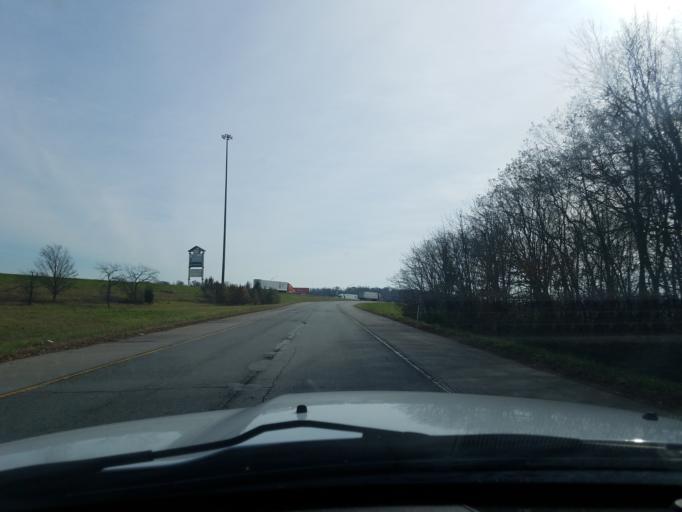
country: US
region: Indiana
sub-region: Delaware County
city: Daleville
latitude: 40.1127
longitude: -85.5702
